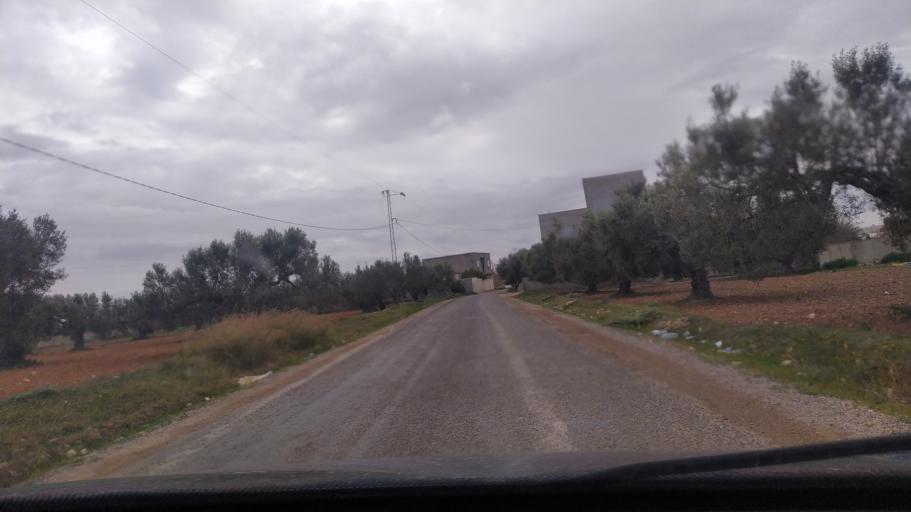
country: TN
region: Al Munastir
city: Sidi Bin Nur
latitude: 35.5126
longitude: 10.9656
